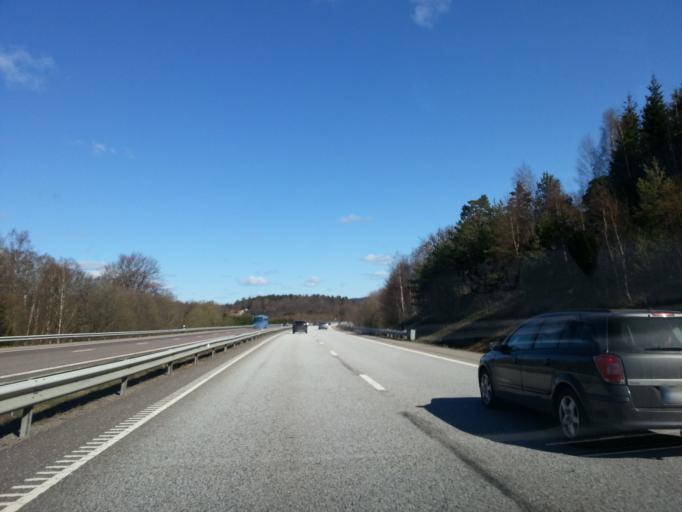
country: SE
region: Vaestra Goetaland
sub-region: Uddevalla Kommun
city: Ljungskile
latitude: 58.1973
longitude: 11.9074
